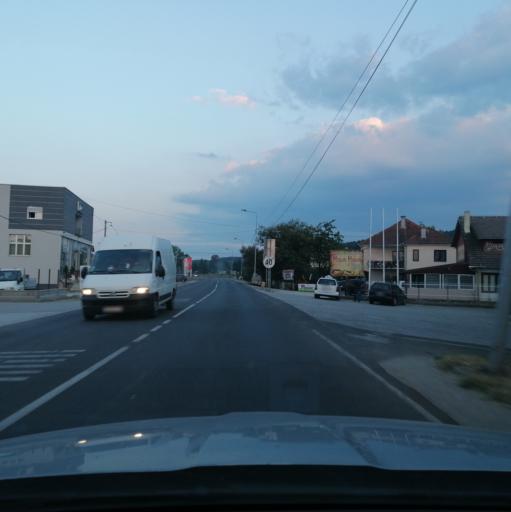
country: RS
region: Central Serbia
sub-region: Raski Okrug
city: Kraljevo
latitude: 43.7055
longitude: 20.7033
